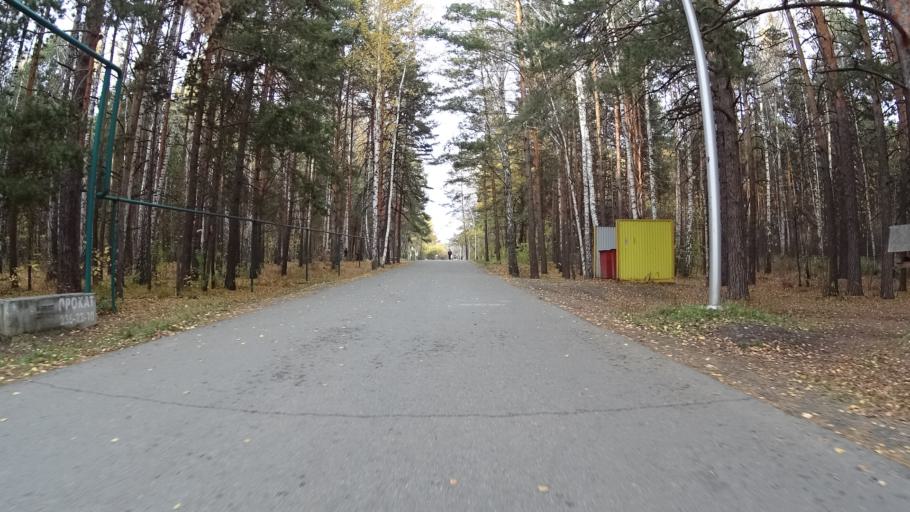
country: RU
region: Chelyabinsk
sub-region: Gorod Chelyabinsk
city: Chelyabinsk
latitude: 55.1450
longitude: 61.3523
